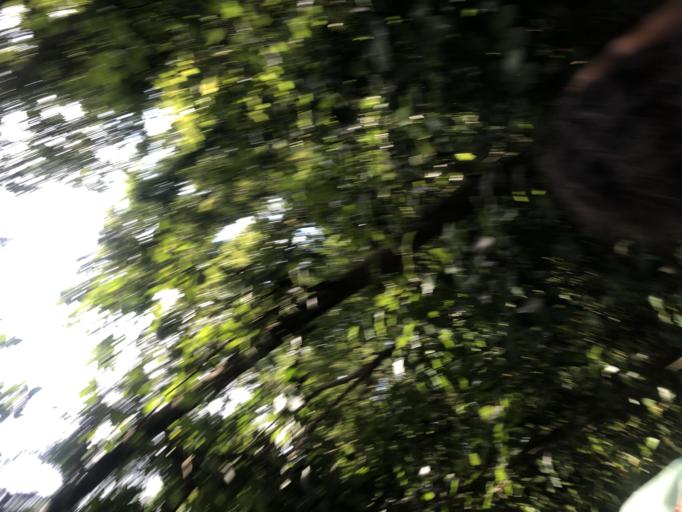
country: NP
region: Far Western
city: Tikapur
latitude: 28.5647
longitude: 81.2765
